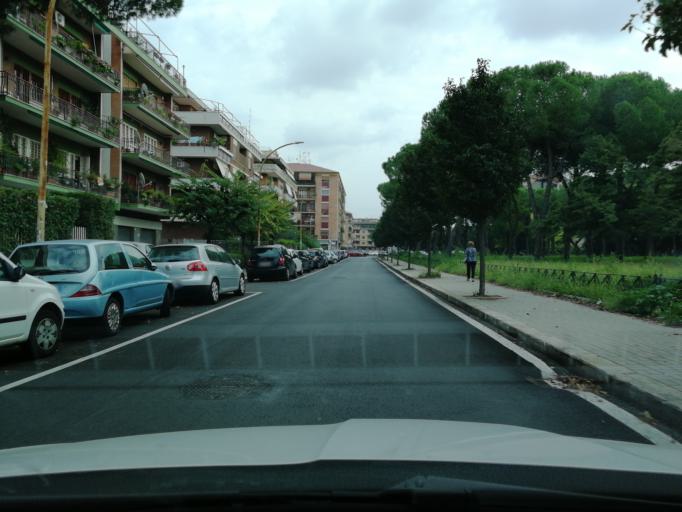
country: IT
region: Latium
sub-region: Citta metropolitana di Roma Capitale
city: Rome
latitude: 41.8543
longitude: 12.5564
